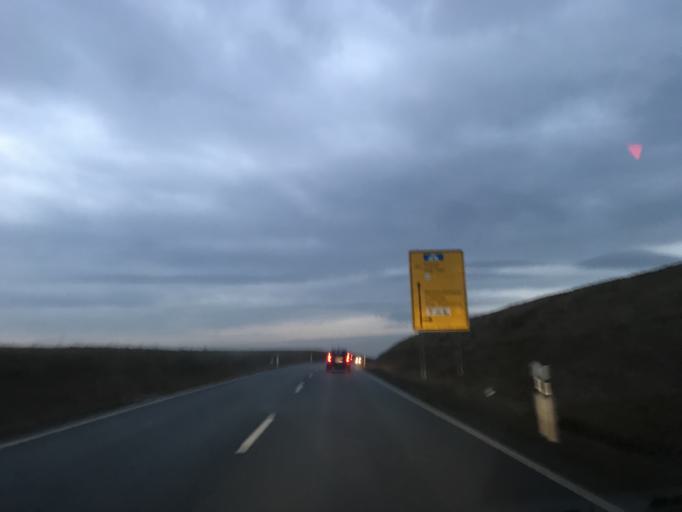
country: DE
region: Hesse
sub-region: Regierungsbezirk Kassel
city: Hofgeismar
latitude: 51.4967
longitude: 9.4069
